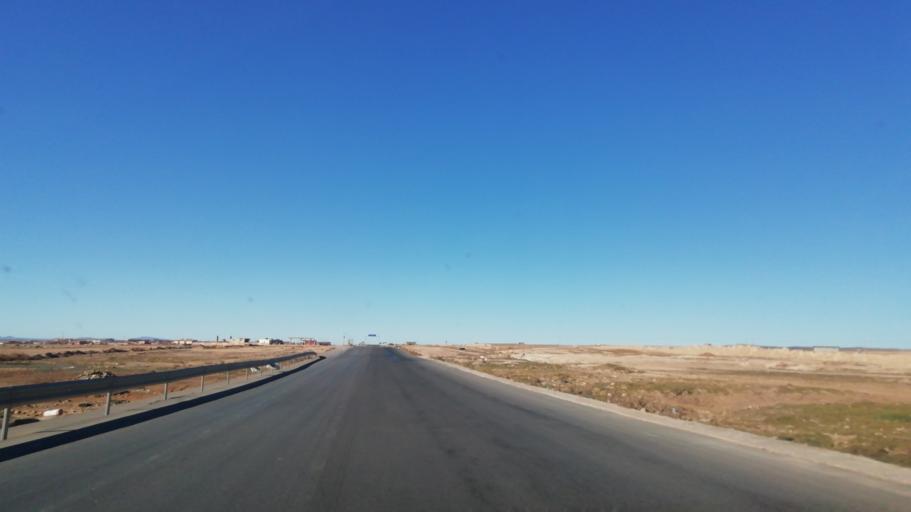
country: DZ
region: Tlemcen
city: Sebdou
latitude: 34.2055
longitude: -1.2388
